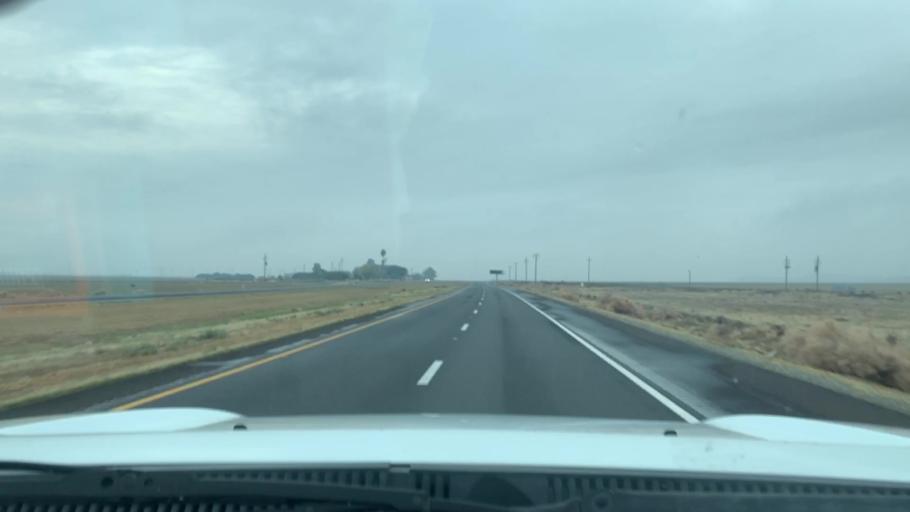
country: US
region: California
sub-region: Kern County
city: Lost Hills
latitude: 35.6421
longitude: -120.0225
